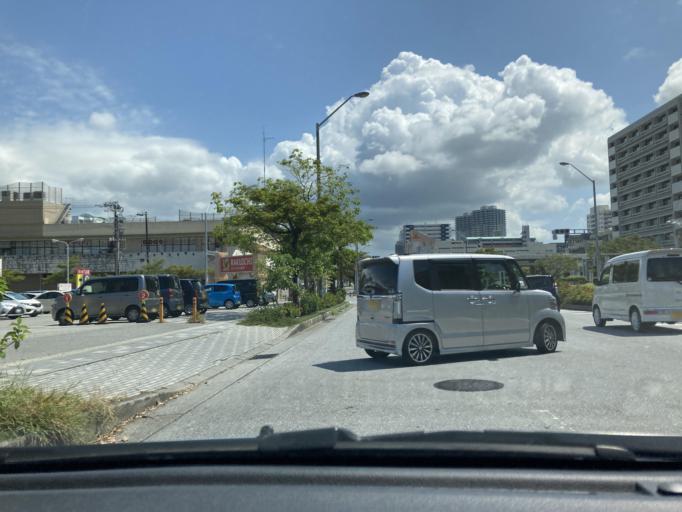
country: JP
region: Okinawa
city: Naha-shi
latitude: 26.2291
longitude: 127.6906
